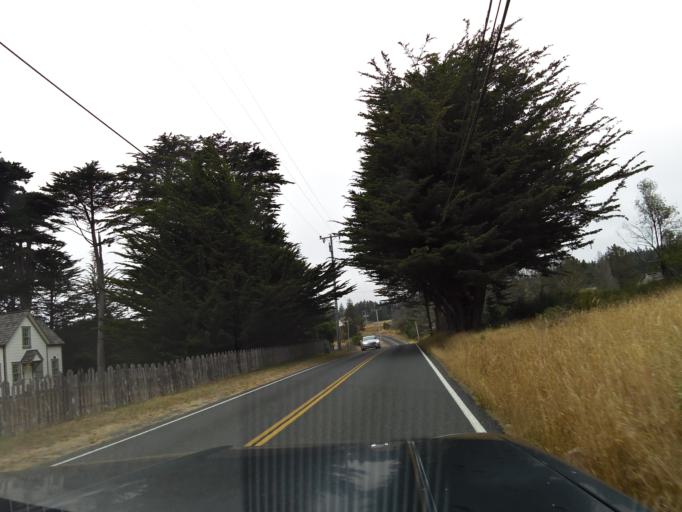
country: US
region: California
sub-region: Mendocino County
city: Fort Bragg
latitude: 39.3494
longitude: -123.8127
